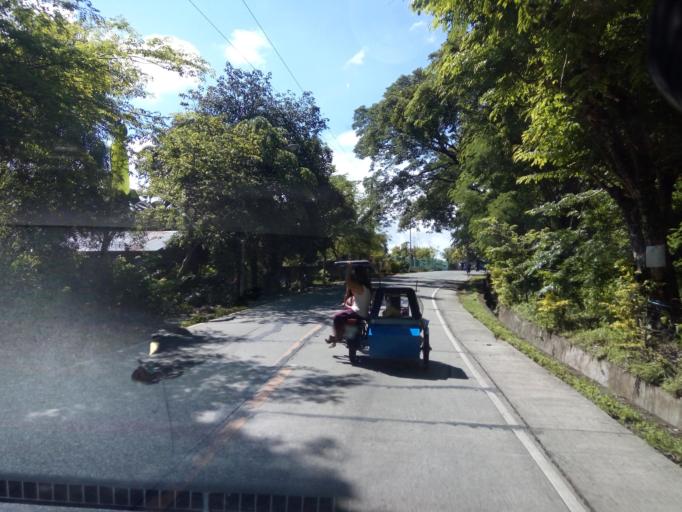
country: PH
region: Central Luzon
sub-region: Province of Nueva Ecija
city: Pantabangan
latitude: 15.8042
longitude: 121.1509
